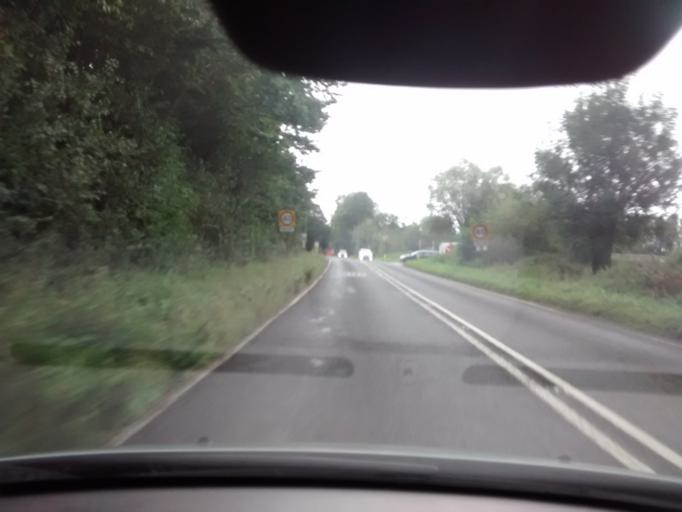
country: GB
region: England
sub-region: Hampshire
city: Fordingbridge
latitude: 50.8870
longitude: -1.7874
